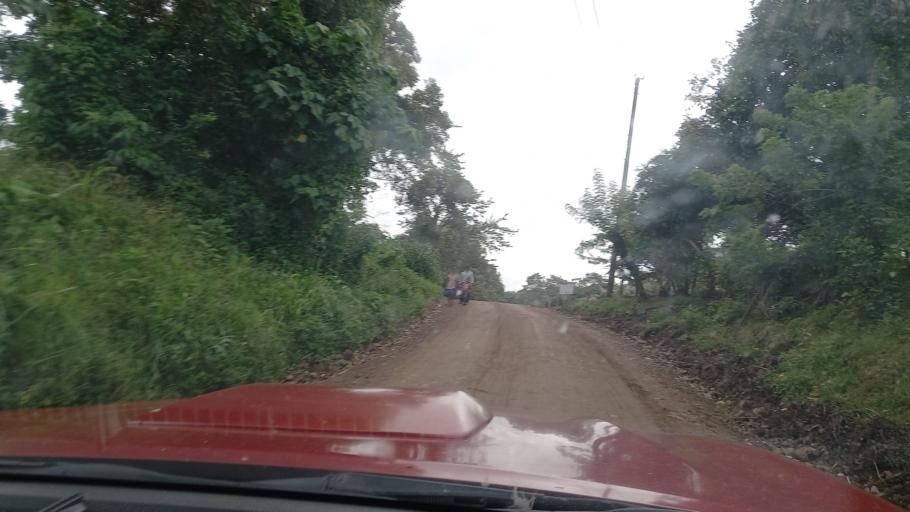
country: NI
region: Jinotega
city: San Jose de Bocay
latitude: 13.3507
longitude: -85.6614
